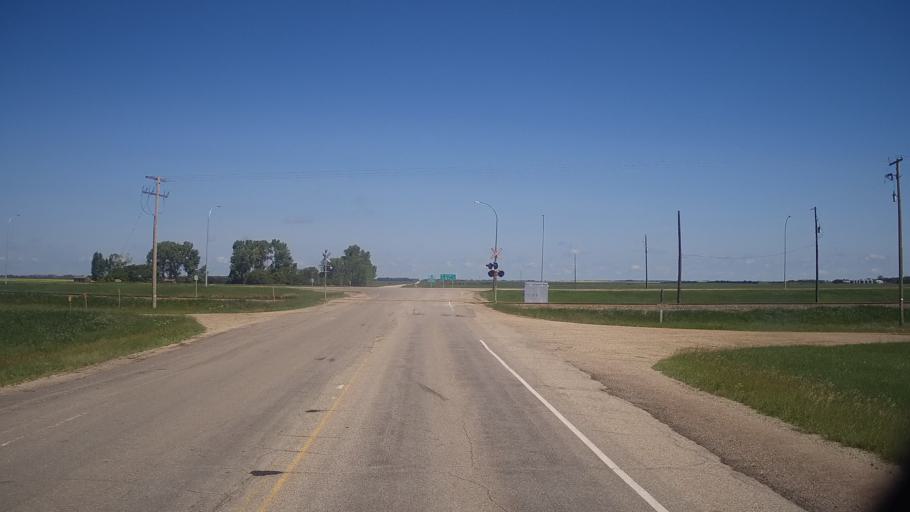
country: CA
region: Saskatchewan
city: Saskatoon
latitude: 51.9902
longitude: -106.0755
